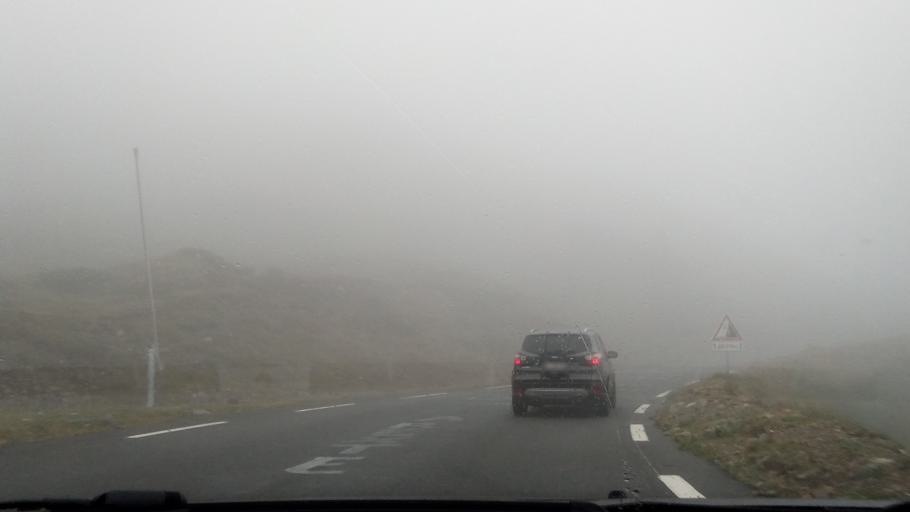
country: FR
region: Midi-Pyrenees
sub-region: Departement des Hautes-Pyrenees
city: Campan
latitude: 42.9048
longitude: 0.1300
